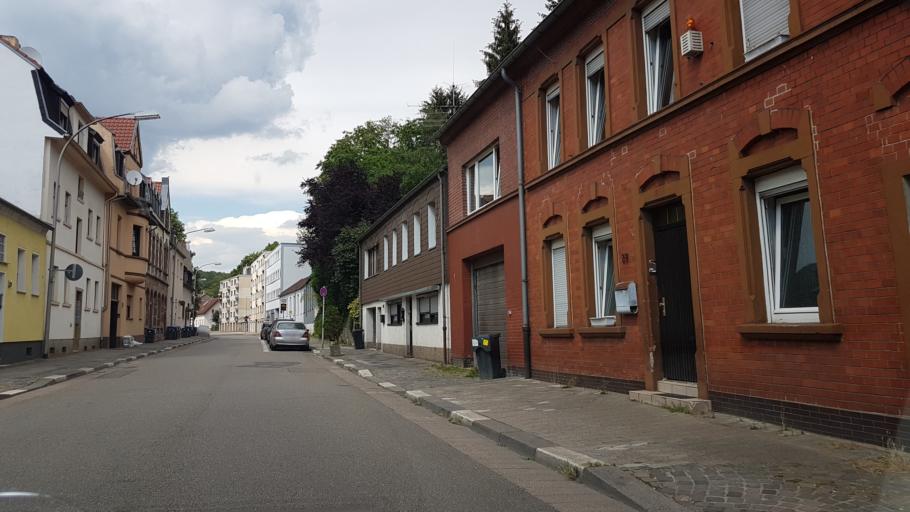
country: DE
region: Saarland
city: Saarbrucken
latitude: 49.2569
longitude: 6.9752
